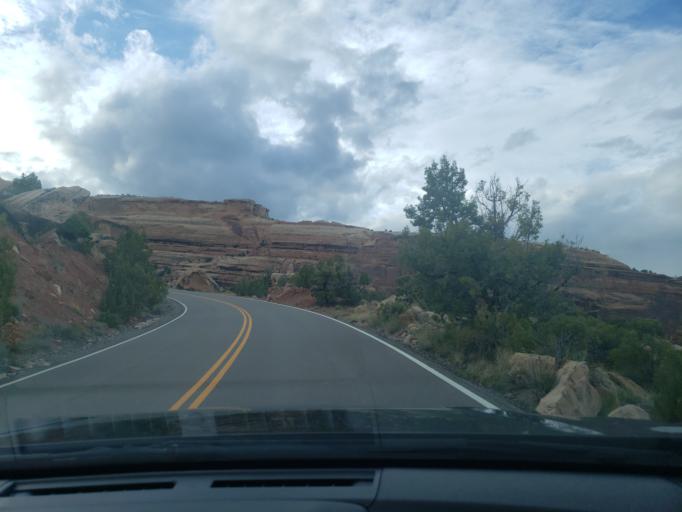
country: US
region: Colorado
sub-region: Mesa County
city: Redlands
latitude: 39.0277
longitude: -108.6413
